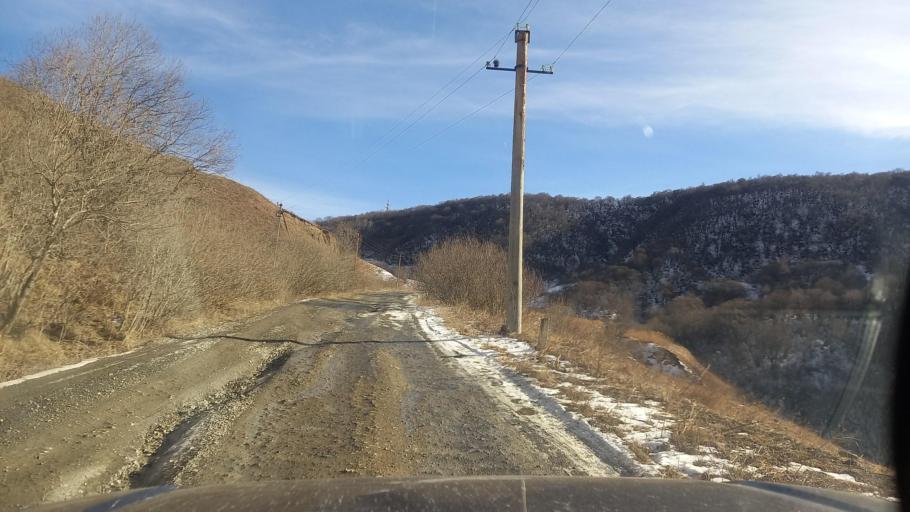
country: RU
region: North Ossetia
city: Verkhniy Fiagdon
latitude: 42.8358
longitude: 44.4710
